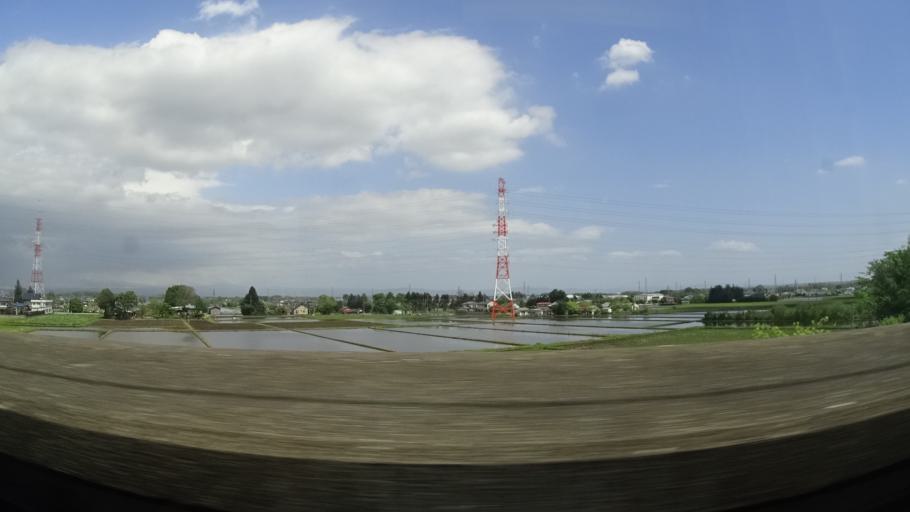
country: JP
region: Tochigi
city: Yaita
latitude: 36.8485
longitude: 139.9643
